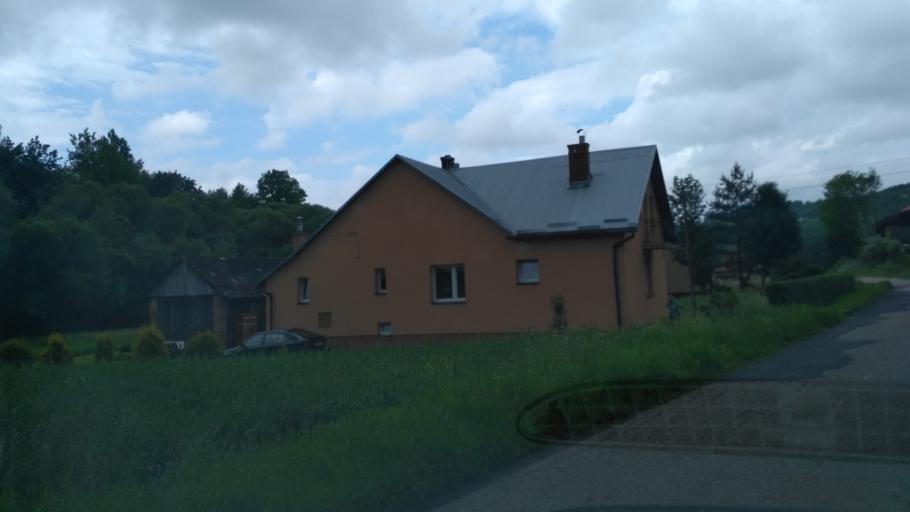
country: PL
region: Subcarpathian Voivodeship
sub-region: Powiat przemyski
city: Dubiecko
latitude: 49.8395
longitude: 22.4061
